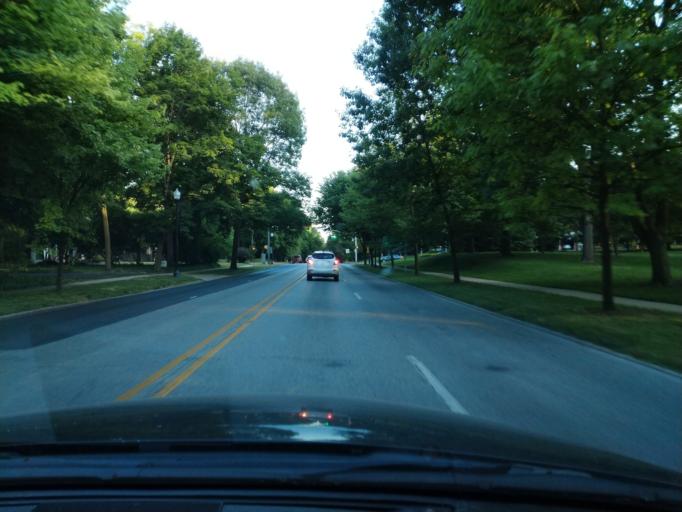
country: US
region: Indiana
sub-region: Marion County
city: Broad Ripple
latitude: 39.8403
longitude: -86.1571
